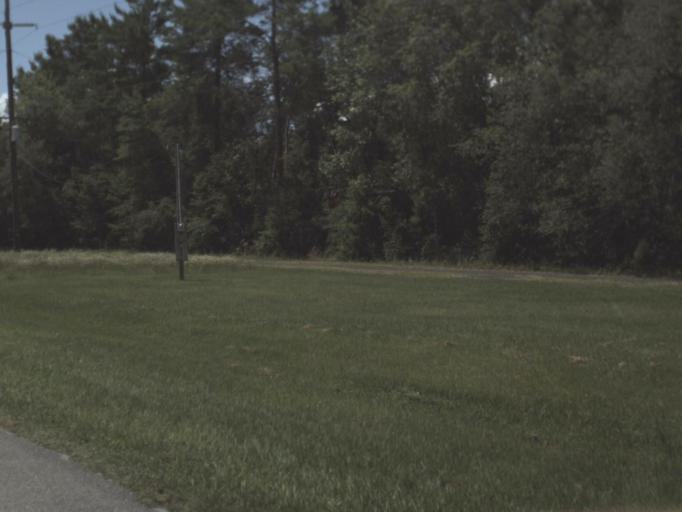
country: US
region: Florida
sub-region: Putnam County
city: Crescent City
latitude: 29.5124
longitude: -81.6121
